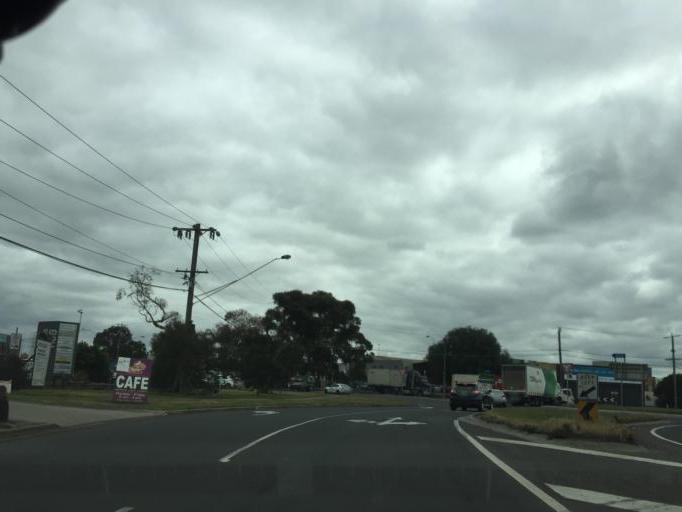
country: AU
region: Victoria
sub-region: Brimbank
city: Brooklyn
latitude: -37.8167
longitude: 144.8171
